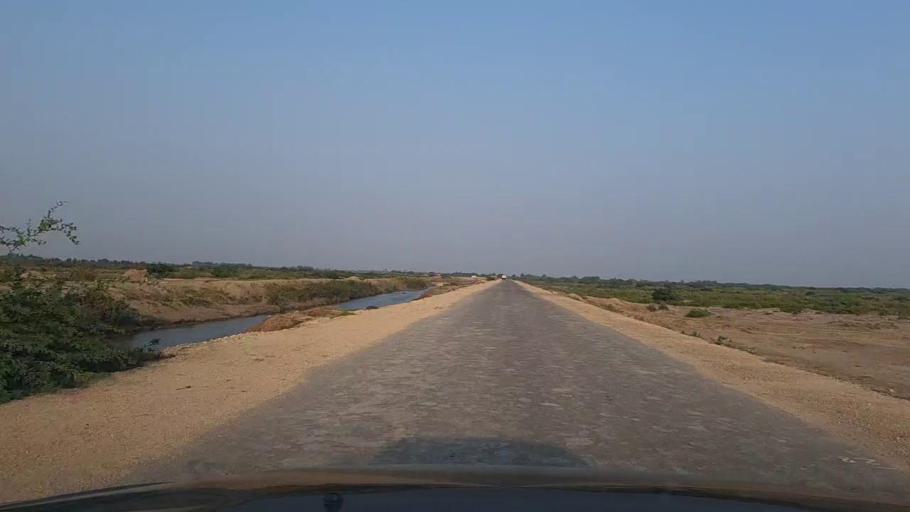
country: PK
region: Sindh
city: Mirpur Sakro
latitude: 24.4429
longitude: 67.7824
